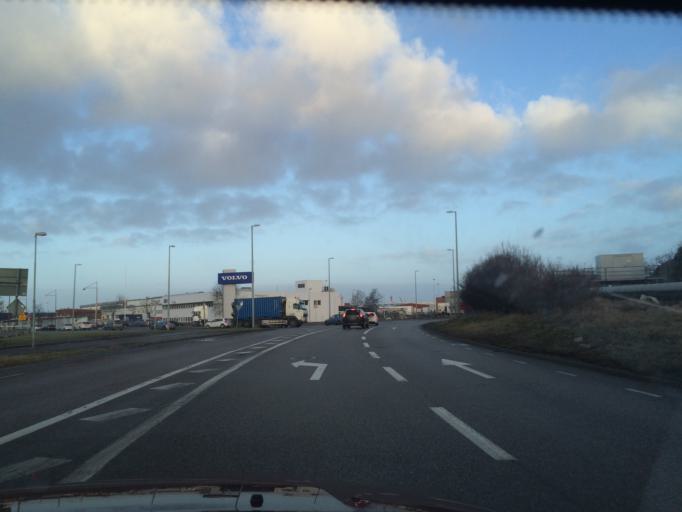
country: SE
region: Vaestra Goetaland
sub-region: Goteborg
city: Torslanda
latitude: 57.6977
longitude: 11.8293
